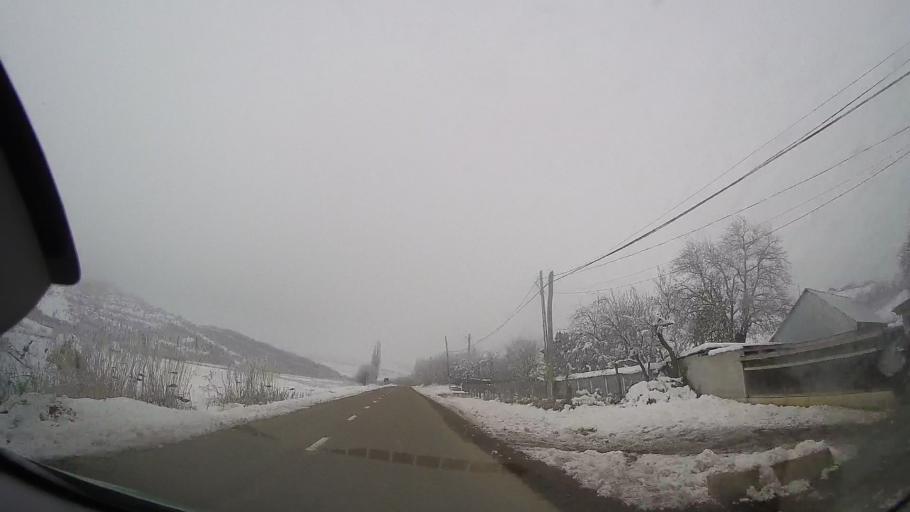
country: RO
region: Neamt
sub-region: Comuna Valea Ursului
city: Valea Ursului
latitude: 46.8018
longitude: 27.1124
